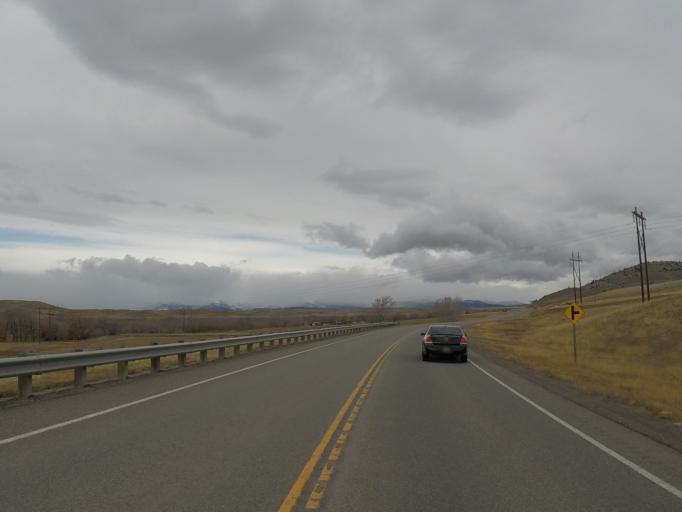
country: US
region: Montana
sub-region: Sweet Grass County
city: Big Timber
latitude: 45.8699
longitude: -109.9447
